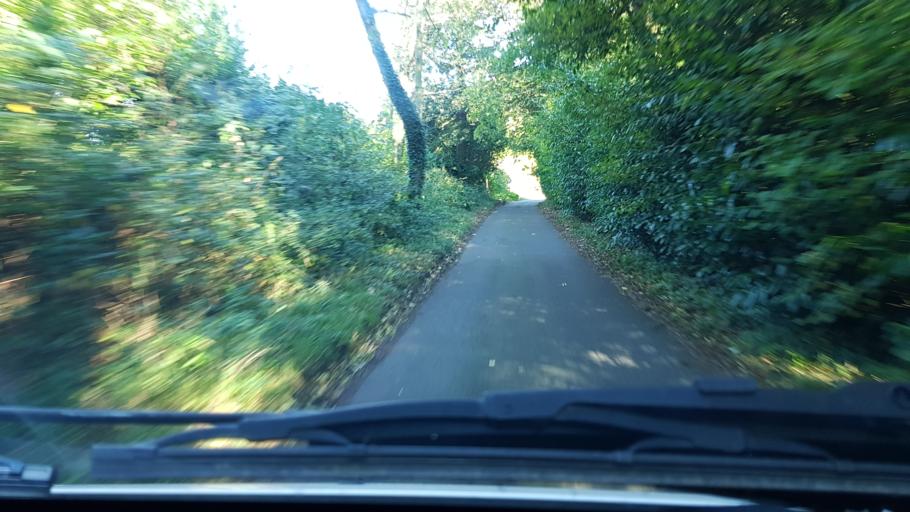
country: GB
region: England
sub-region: Surrey
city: Ockley
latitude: 51.1419
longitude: -0.3357
